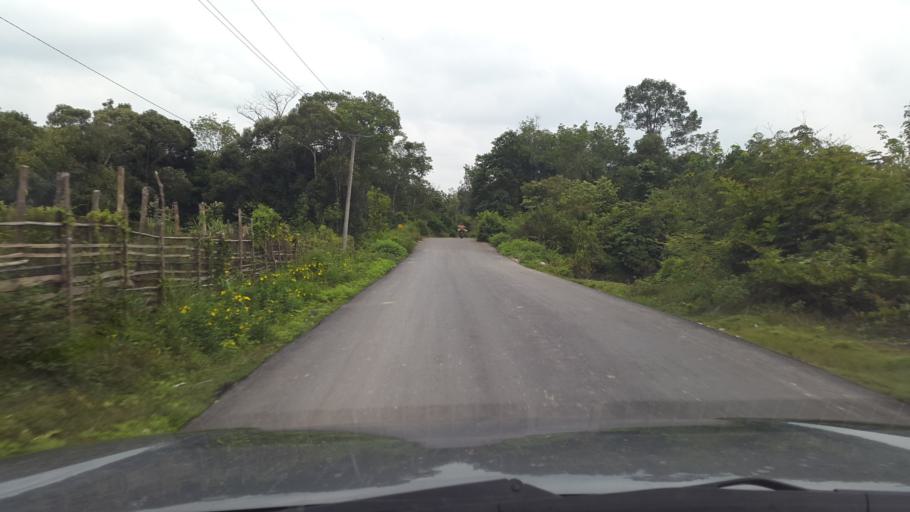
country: ID
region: South Sumatra
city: Gunungmenang
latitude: -3.0989
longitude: 103.9143
